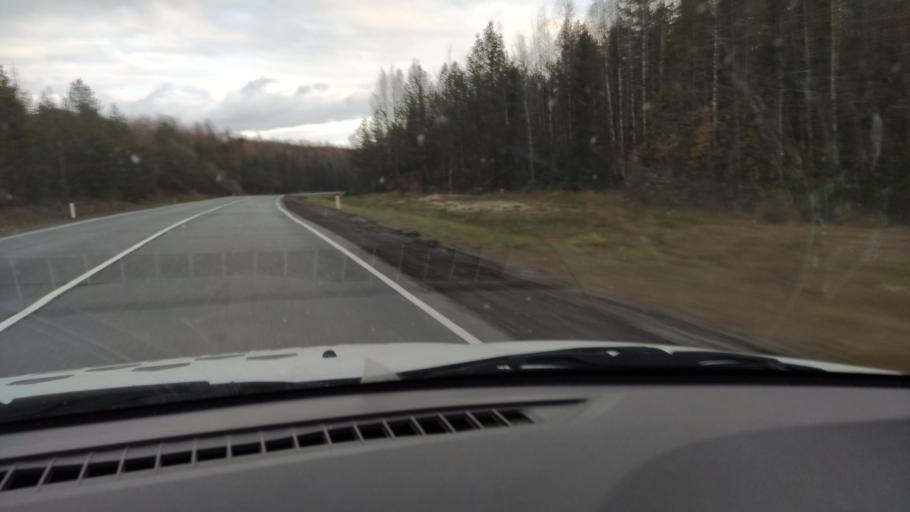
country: RU
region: Kirov
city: Omutninsk
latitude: 58.7510
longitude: 52.0554
